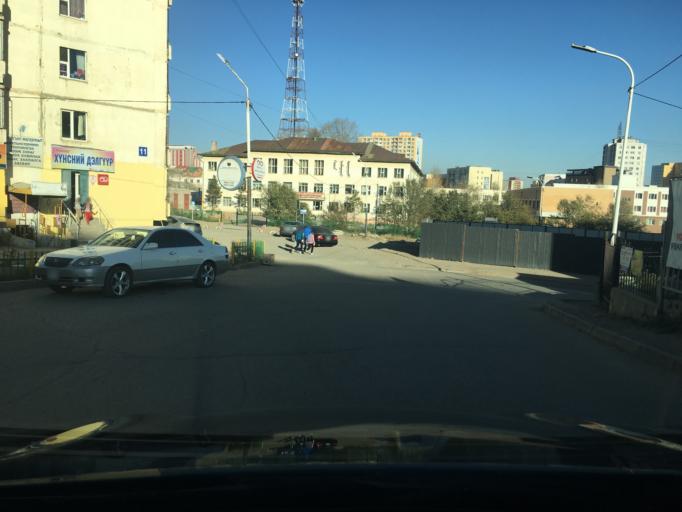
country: MN
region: Ulaanbaatar
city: Ulaanbaatar
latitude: 47.9268
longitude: 106.8823
